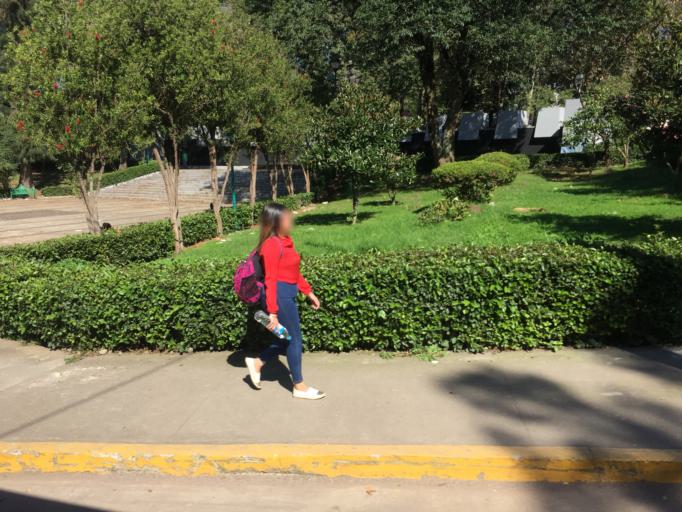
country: MX
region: Veracruz
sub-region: Xalapa
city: Xalapa de Enriquez
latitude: 19.5441
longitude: -96.9276
